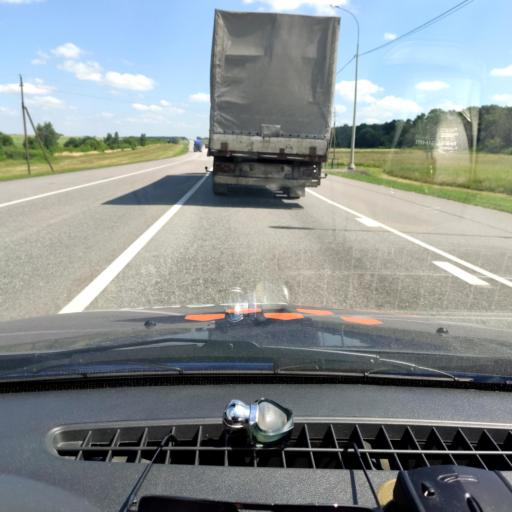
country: RU
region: Orjol
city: Orel
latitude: 52.8578
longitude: 36.2041
